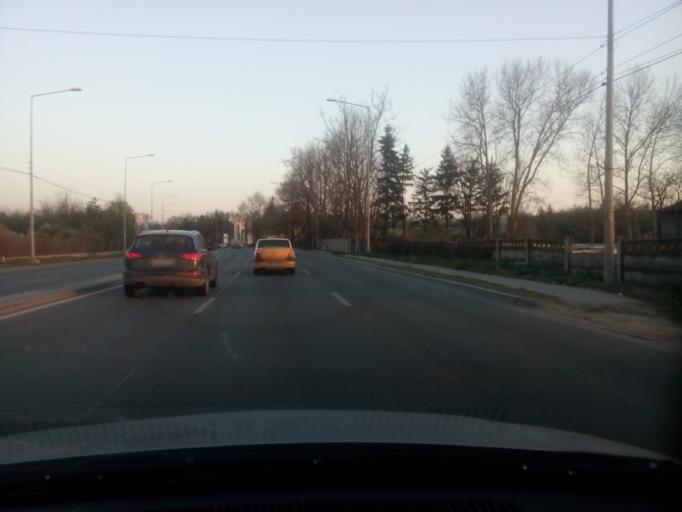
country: RO
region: Ilfov
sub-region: Comuna Otopeni
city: Otopeni
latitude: 44.5269
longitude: 26.0710
